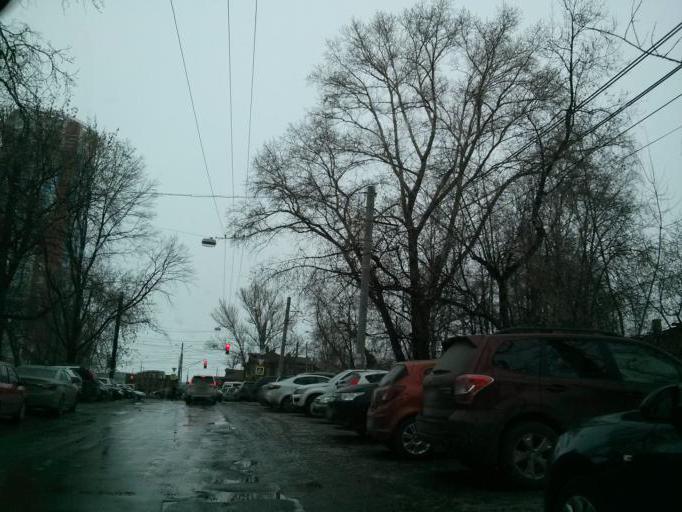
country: RU
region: Nizjnij Novgorod
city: Nizhniy Novgorod
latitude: 56.3211
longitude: 44.0376
